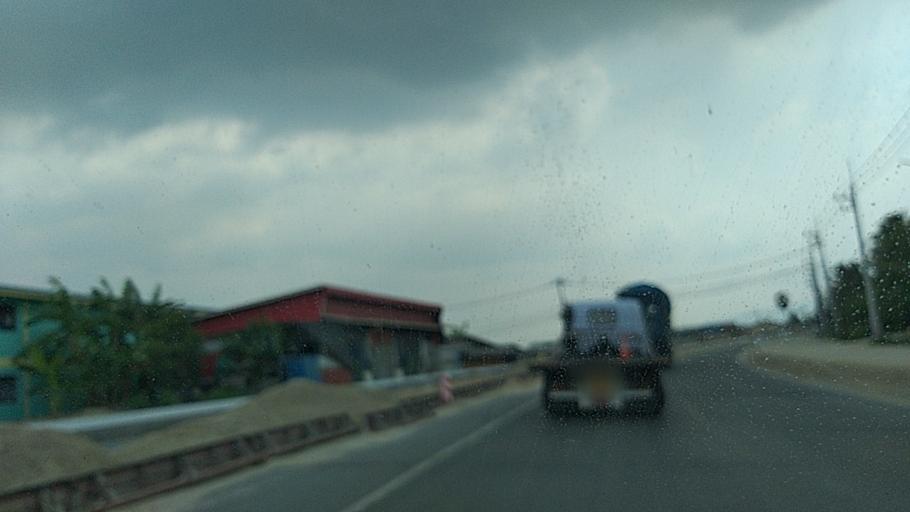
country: TH
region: Chon Buri
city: Ban Bueng
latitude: 13.3125
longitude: 101.1841
